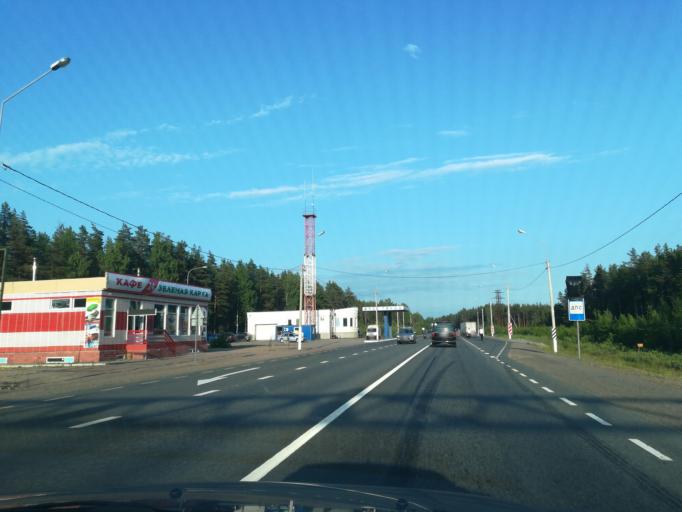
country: RU
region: Leningrad
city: Vyborg
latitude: 60.6645
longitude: 28.9296
